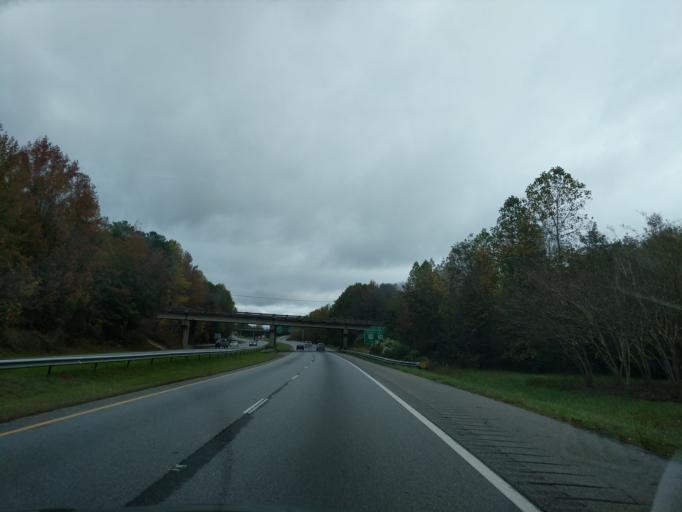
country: US
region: North Carolina
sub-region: Cleveland County
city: Kings Mountain
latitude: 35.2354
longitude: -81.3159
